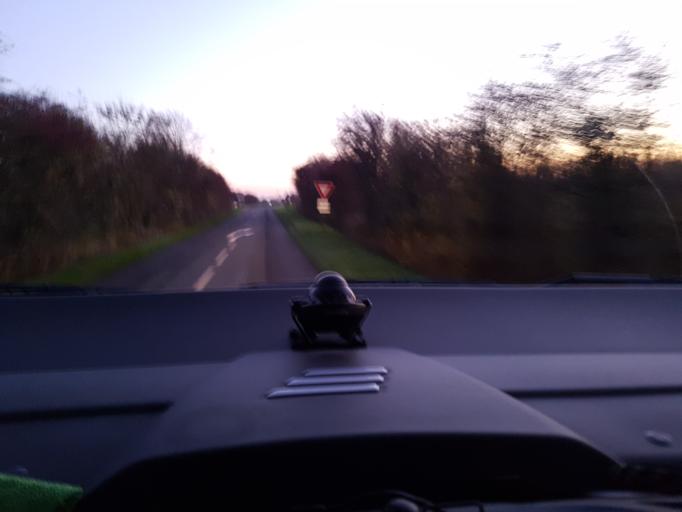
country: FR
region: Picardie
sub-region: Departement de la Somme
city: Saint-Valery-sur-Somme
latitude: 50.1990
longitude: 1.6932
